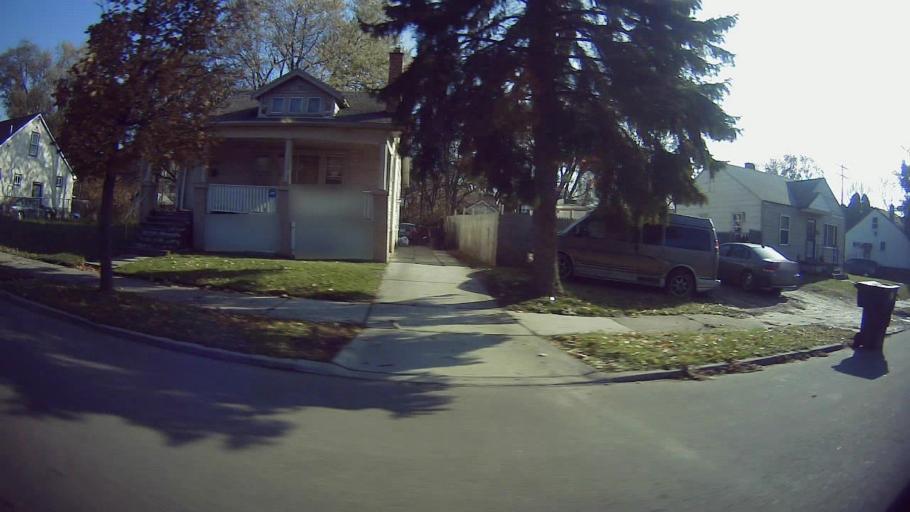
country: US
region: Michigan
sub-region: Wayne County
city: Dearborn
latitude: 42.3777
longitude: -83.1683
